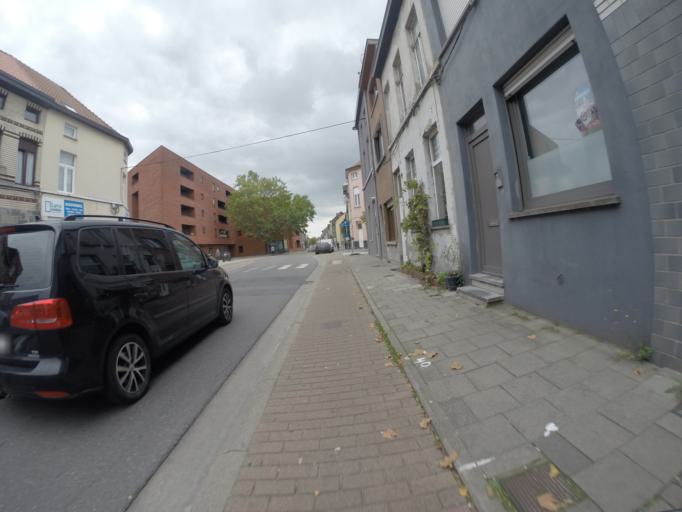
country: BE
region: Flanders
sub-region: Provincie Oost-Vlaanderen
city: Gent
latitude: 51.0764
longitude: 3.7302
